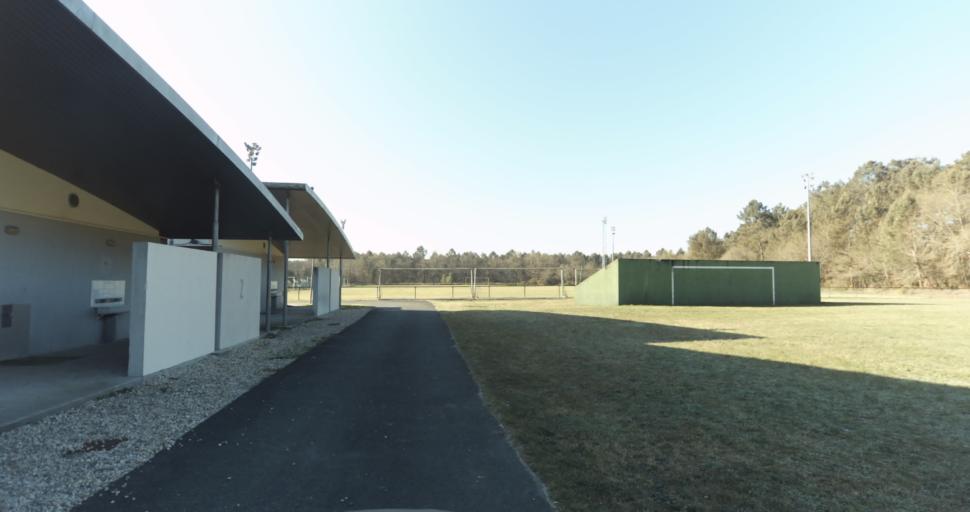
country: FR
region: Aquitaine
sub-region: Departement de la Gironde
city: Martignas-sur-Jalle
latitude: 44.8082
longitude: -0.8000
